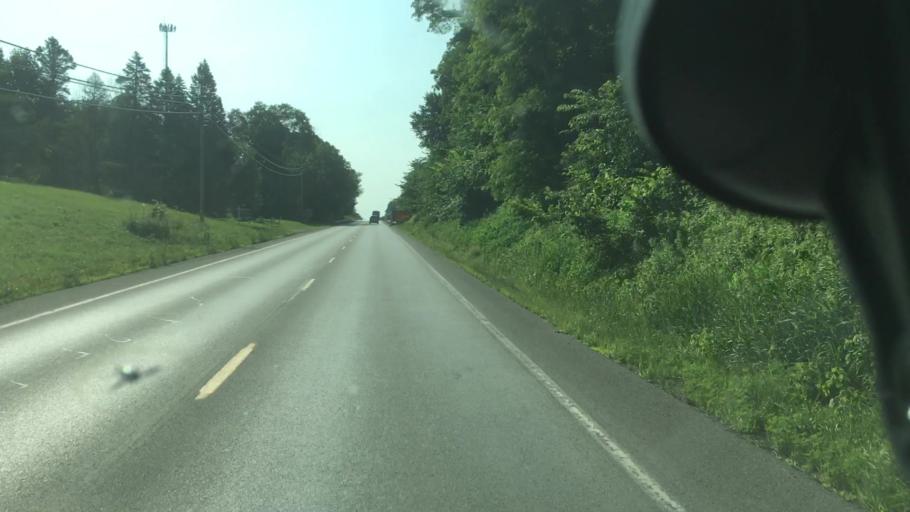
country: US
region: Pennsylvania
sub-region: Lawrence County
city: Bessemer
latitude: 41.0114
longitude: -80.4800
